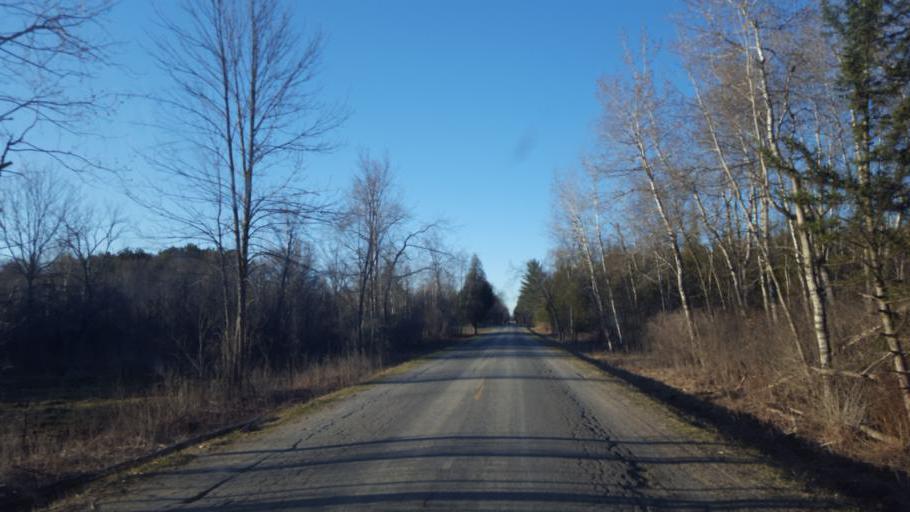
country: US
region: Michigan
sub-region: Mecosta County
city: Canadian Lakes
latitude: 43.5578
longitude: -85.3934
